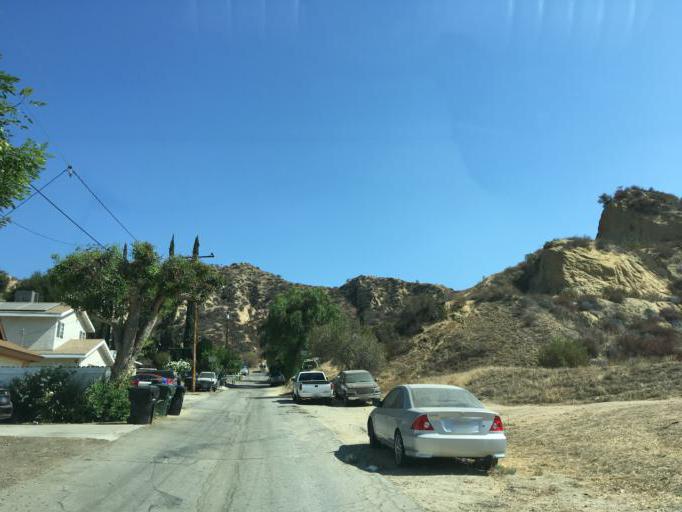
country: US
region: California
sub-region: Los Angeles County
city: Val Verde
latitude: 34.4488
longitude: -118.6669
